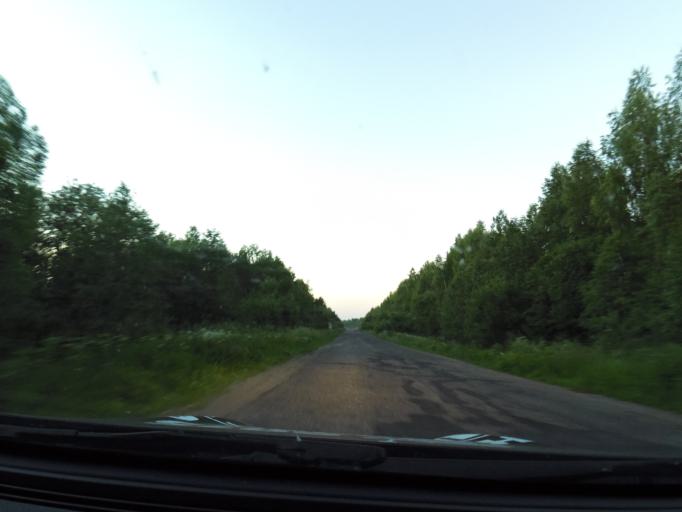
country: RU
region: Kostroma
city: Buy
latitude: 58.4375
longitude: 41.3297
